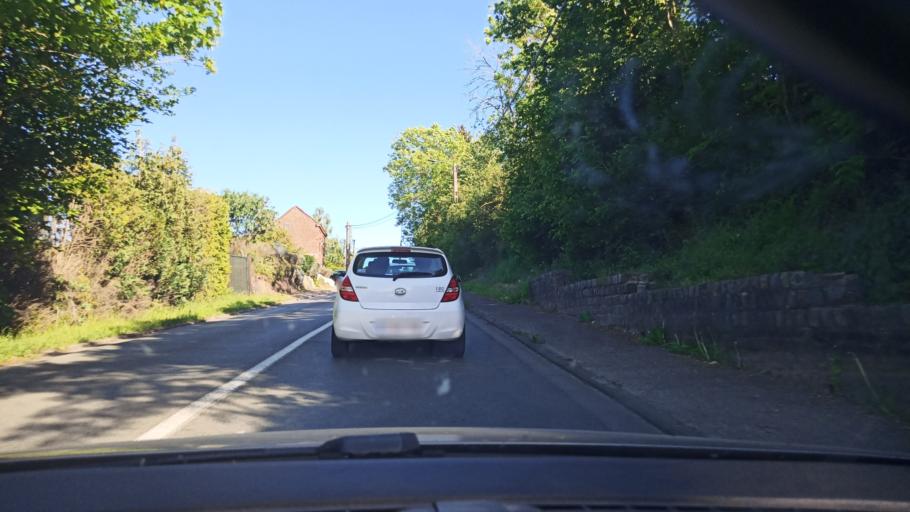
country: BE
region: Wallonia
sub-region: Province du Hainaut
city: Lobbes
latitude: 50.3406
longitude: 4.2655
